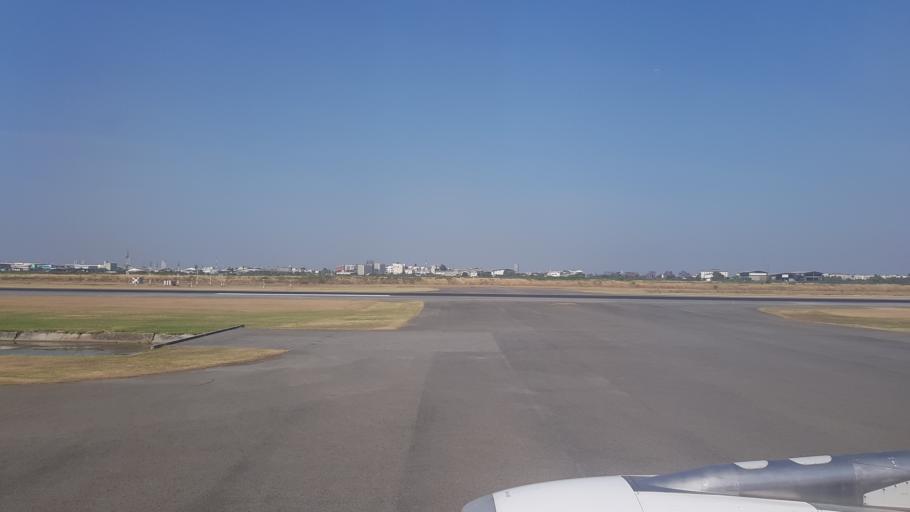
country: TH
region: Bangkok
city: Lat Krabang
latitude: 13.6750
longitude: 100.7375
